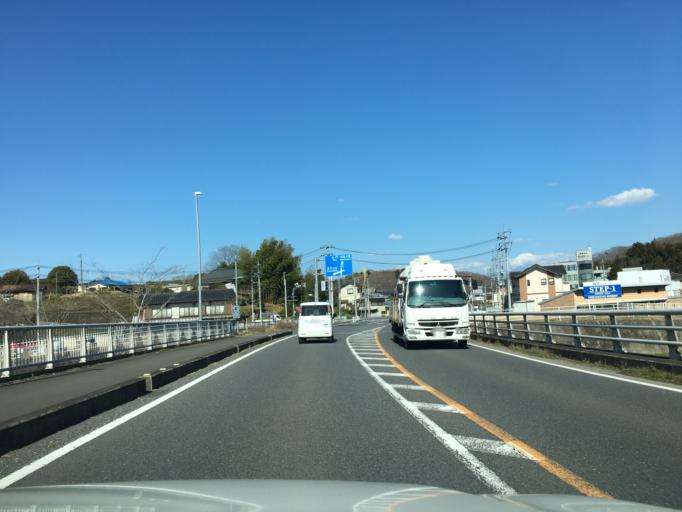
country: JP
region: Tochigi
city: Motegi
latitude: 36.5310
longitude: 140.2011
